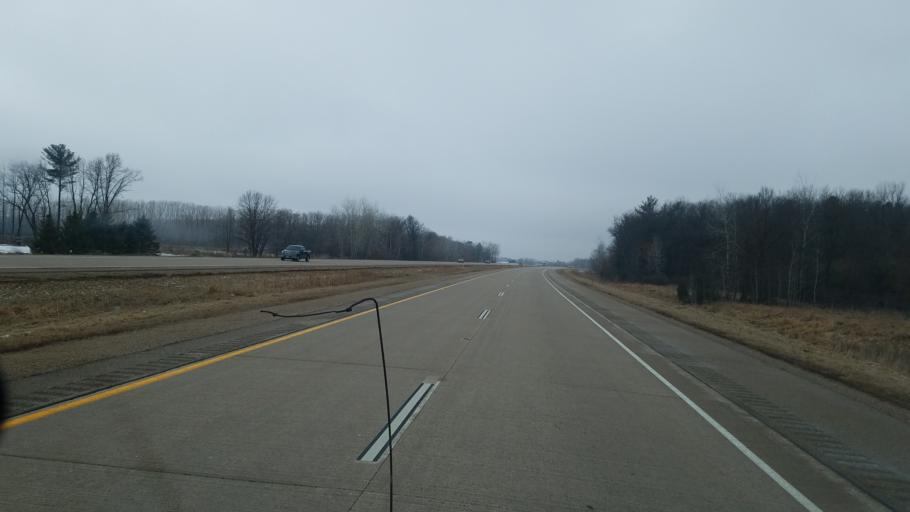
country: US
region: Wisconsin
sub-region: Waupaca County
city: Weyauwega
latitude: 44.2512
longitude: -88.8279
